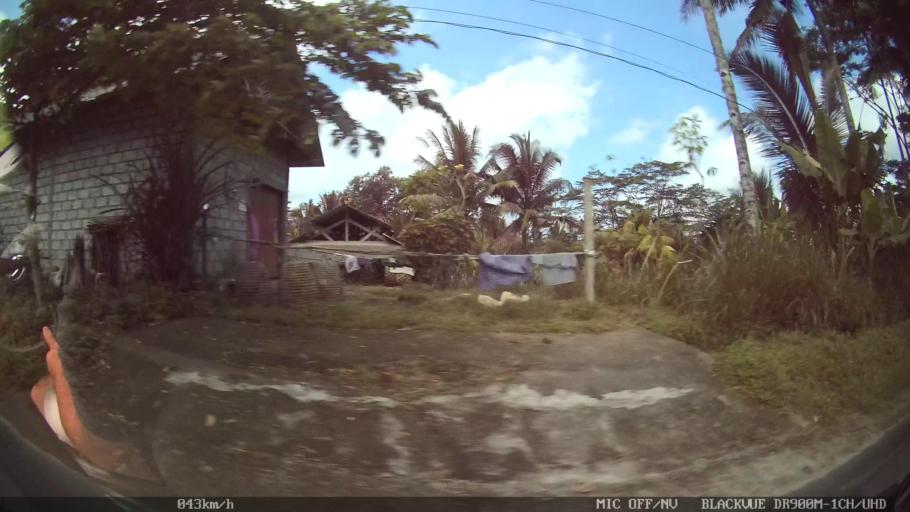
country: ID
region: Bali
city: Banjar Bebalang
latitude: -8.4744
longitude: 115.3423
